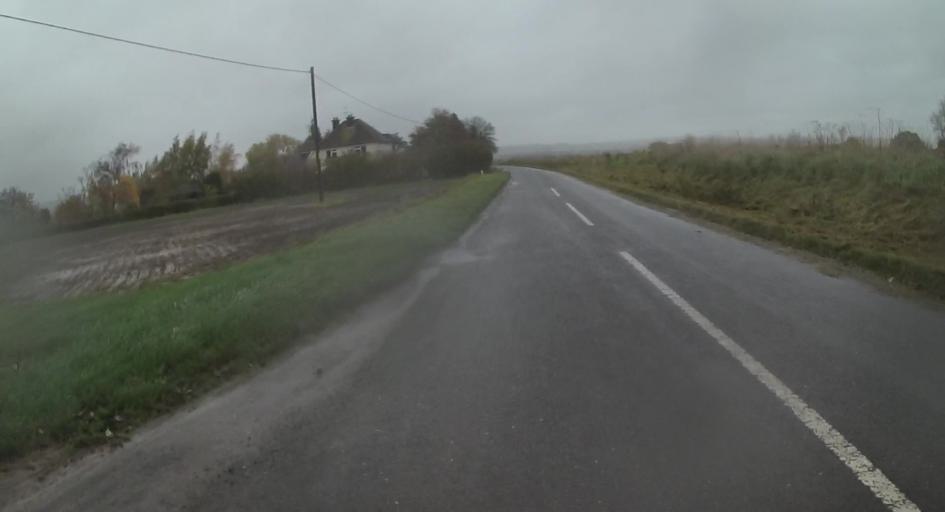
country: GB
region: England
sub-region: Hampshire
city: Kingsley
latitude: 51.1666
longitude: -0.8996
